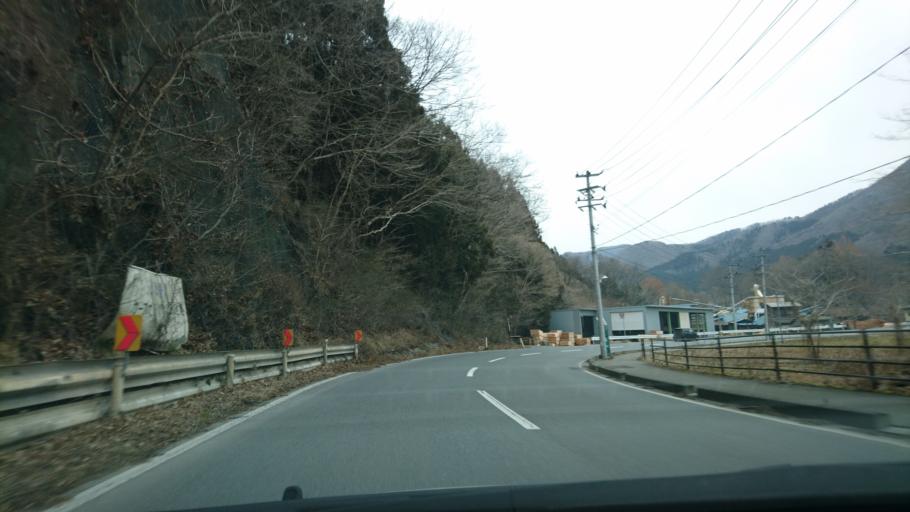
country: JP
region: Iwate
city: Tono
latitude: 39.1972
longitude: 141.5850
